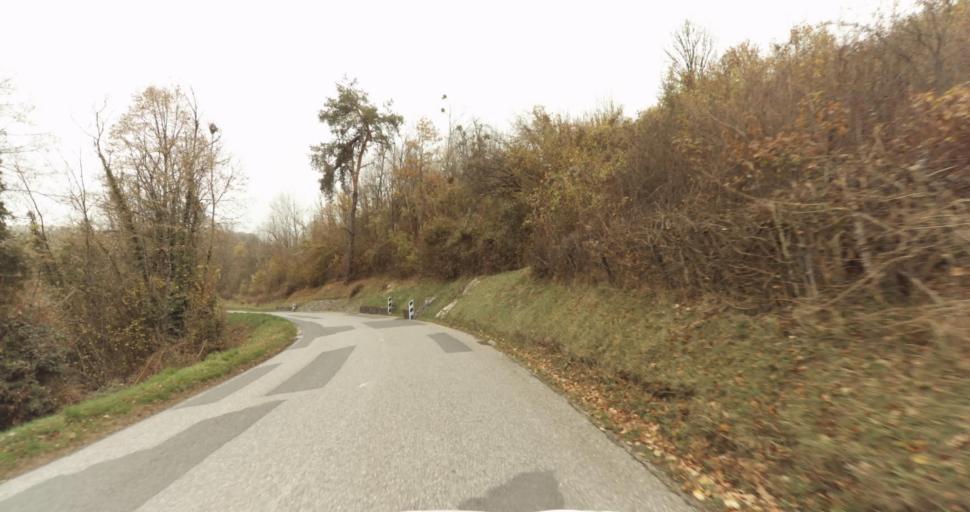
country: FR
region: Rhone-Alpes
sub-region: Departement de la Haute-Savoie
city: Alby-sur-Cheran
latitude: 45.8163
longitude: 6.0255
